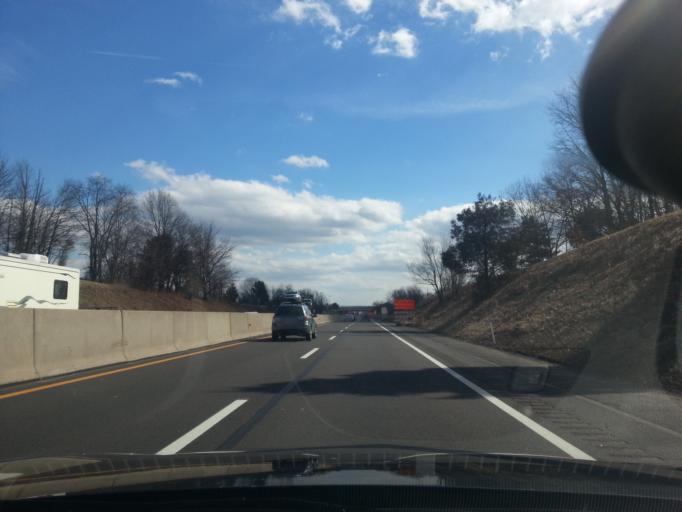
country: US
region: Pennsylvania
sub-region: Montgomery County
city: Harleysville
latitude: 40.2753
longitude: -75.3589
